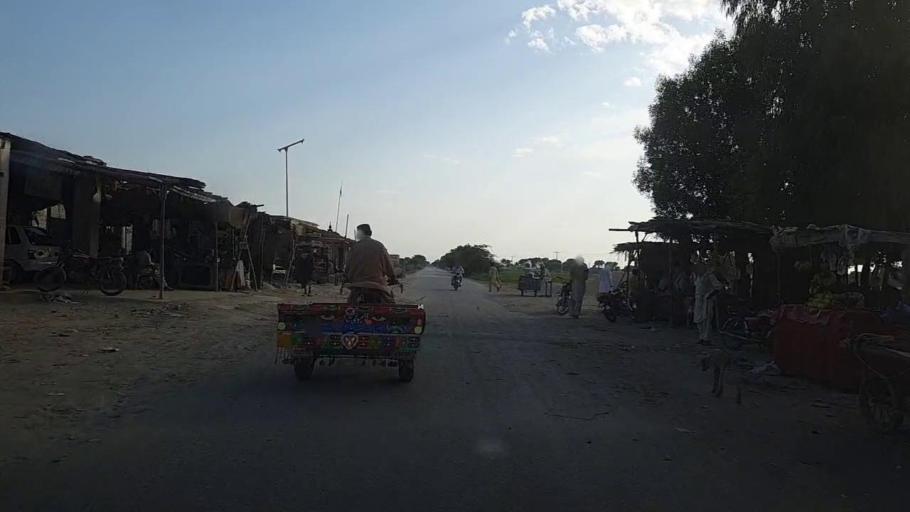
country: PK
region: Sindh
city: Thul
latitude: 28.1937
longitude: 68.7350
